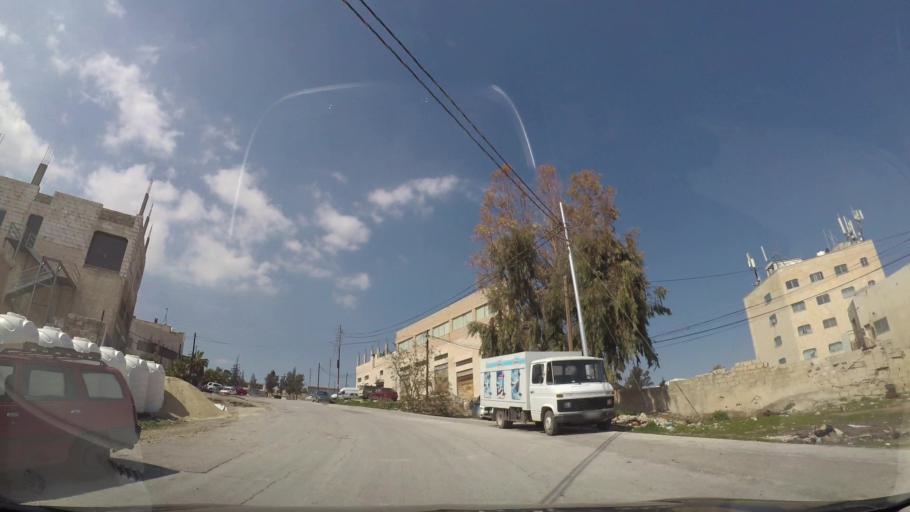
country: JO
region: Zarqa
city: Russeifa
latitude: 31.9904
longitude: 36.0054
